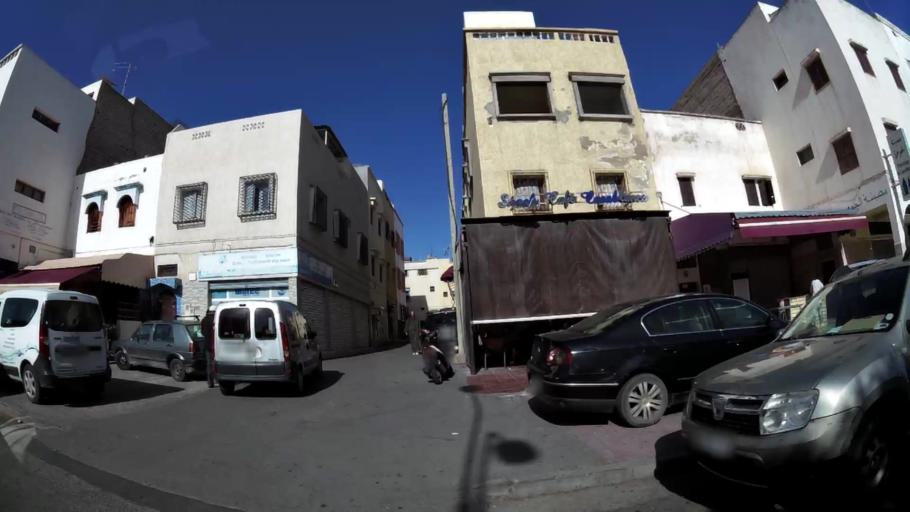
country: MA
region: Oued ed Dahab-Lagouira
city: Dakhla
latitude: 30.4112
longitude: -9.5678
